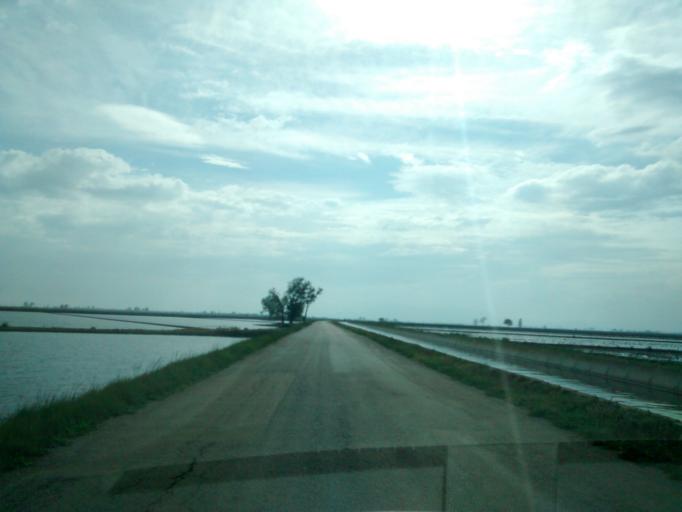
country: ES
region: Catalonia
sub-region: Provincia de Tarragona
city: Deltebre
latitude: 40.6914
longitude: 0.7886
